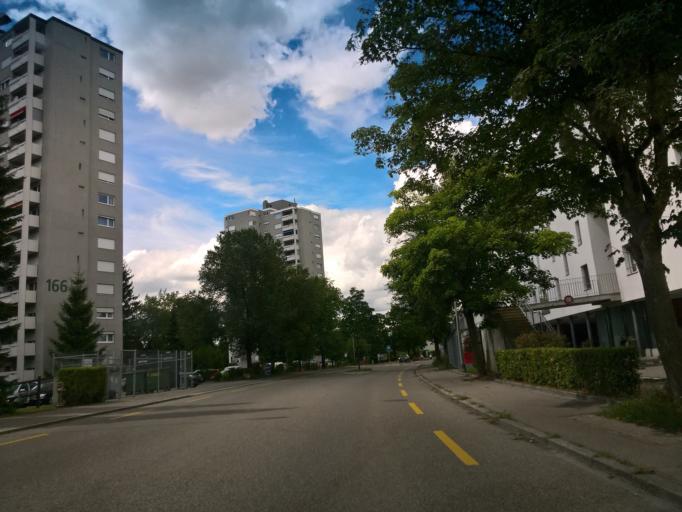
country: CH
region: Zurich
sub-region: Bezirk Buelach
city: Grossacker/Opfikon
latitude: 47.4243
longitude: 8.5755
